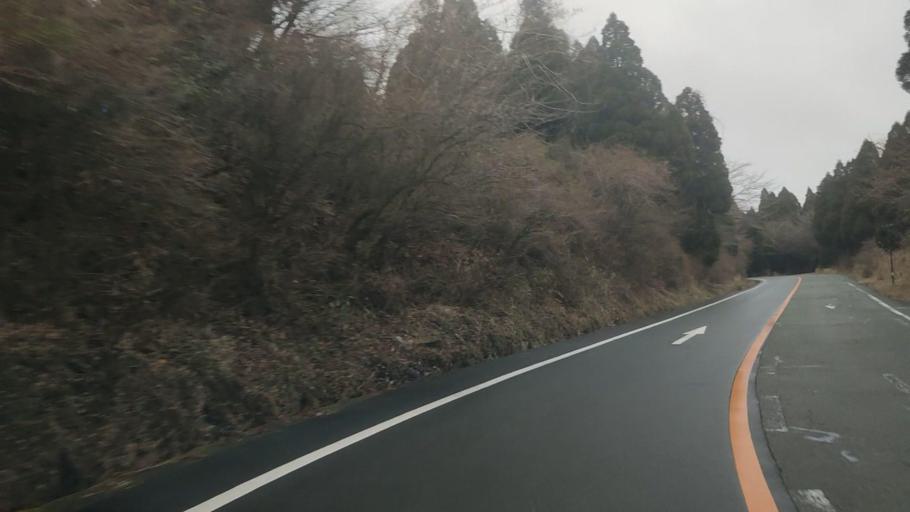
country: JP
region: Kumamoto
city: Aso
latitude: 32.9001
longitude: 131.0467
